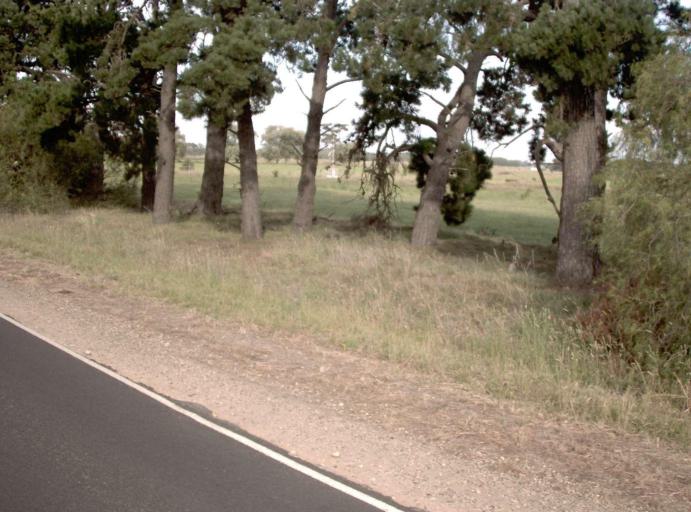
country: AU
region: Victoria
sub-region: Wellington
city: Heyfield
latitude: -38.0161
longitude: 146.7717
